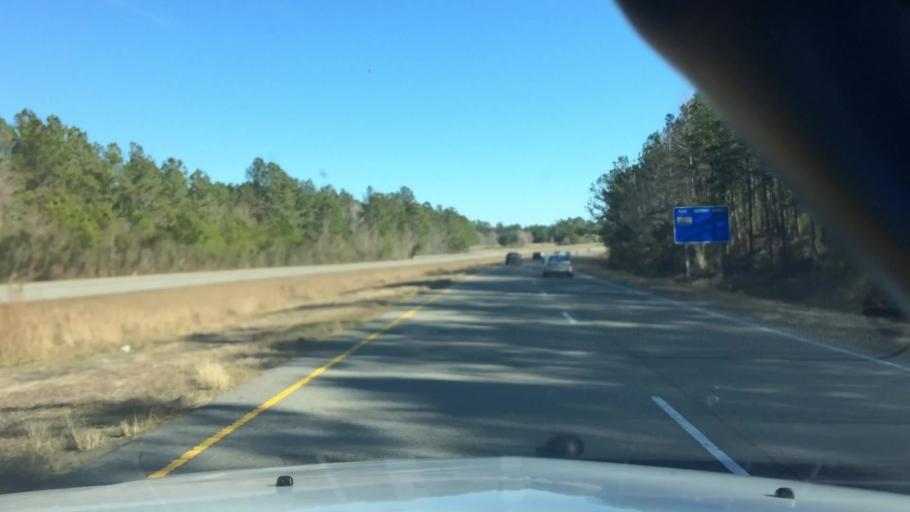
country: US
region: North Carolina
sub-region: Brunswick County
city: Shallotte
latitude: 33.9715
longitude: -78.4103
